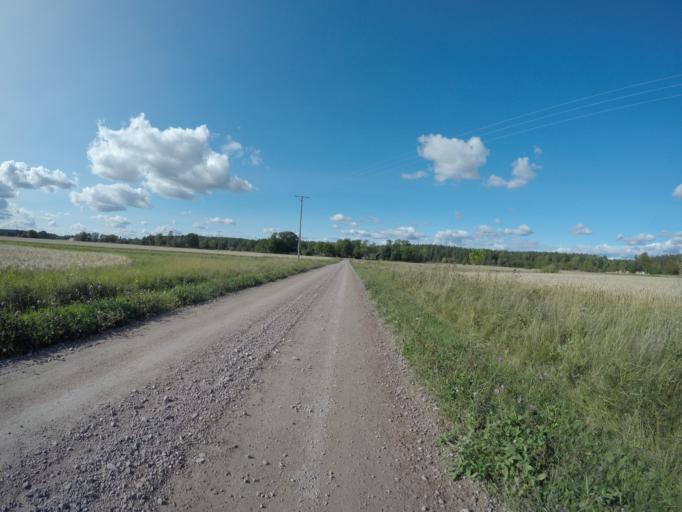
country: SE
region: Soedermanland
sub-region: Eskilstuna Kommun
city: Kvicksund
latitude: 59.5221
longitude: 16.3640
